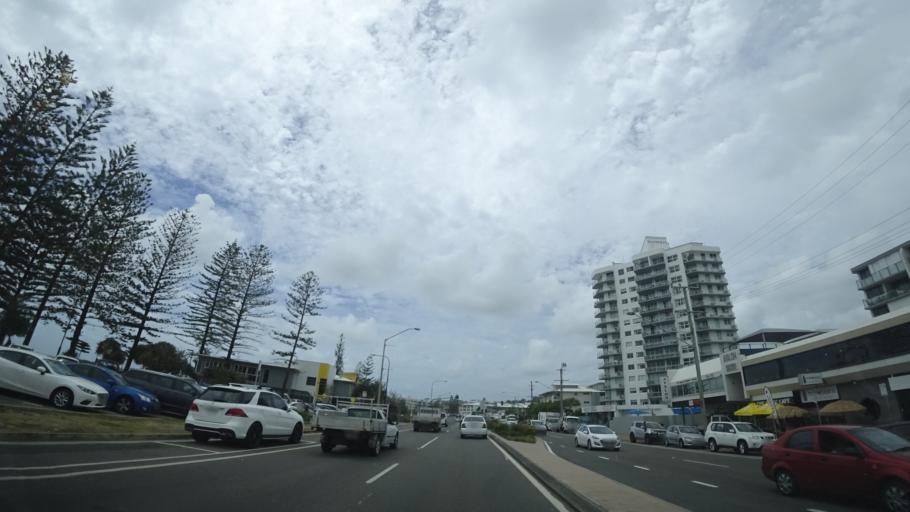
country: AU
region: Queensland
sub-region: Sunshine Coast
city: Mooloolaba
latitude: -26.6679
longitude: 153.1066
